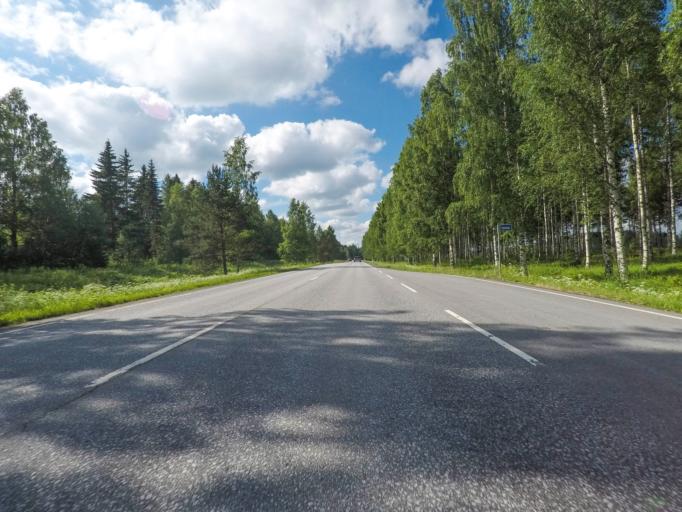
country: FI
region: Southern Savonia
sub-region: Savonlinna
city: Kerimaeki
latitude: 61.8087
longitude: 29.2735
